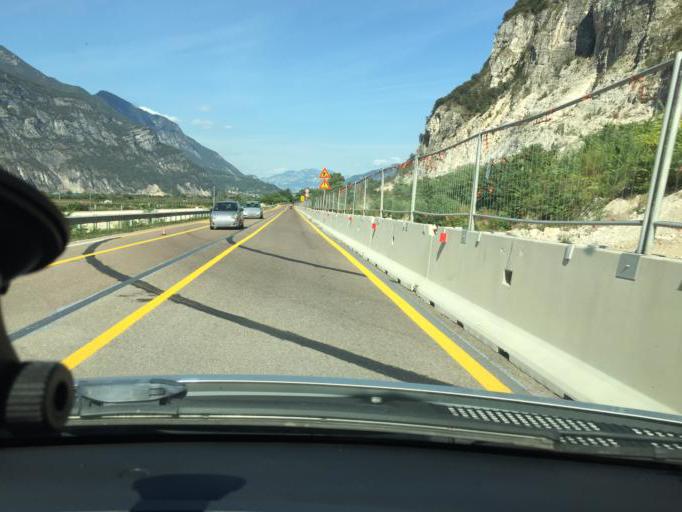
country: IT
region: Trentino-Alto Adige
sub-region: Provincia di Trento
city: Aldeno
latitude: 45.9689
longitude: 11.1131
